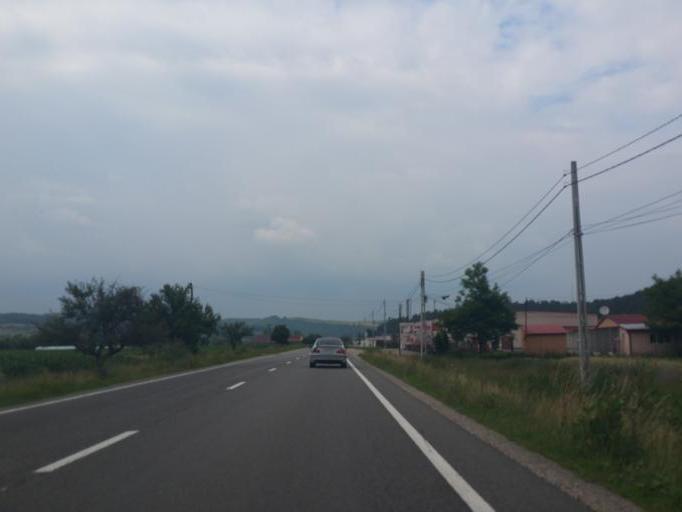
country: RO
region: Salaj
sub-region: Comuna Romanasi
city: Romanasi
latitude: 47.0982
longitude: 23.1880
